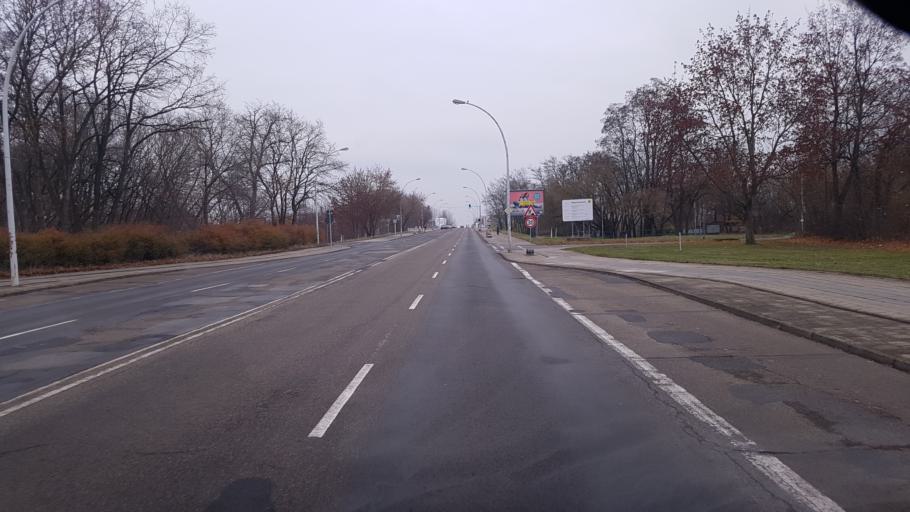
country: DE
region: Brandenburg
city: Eisenhuettenstadt
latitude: 52.1445
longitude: 14.6370
